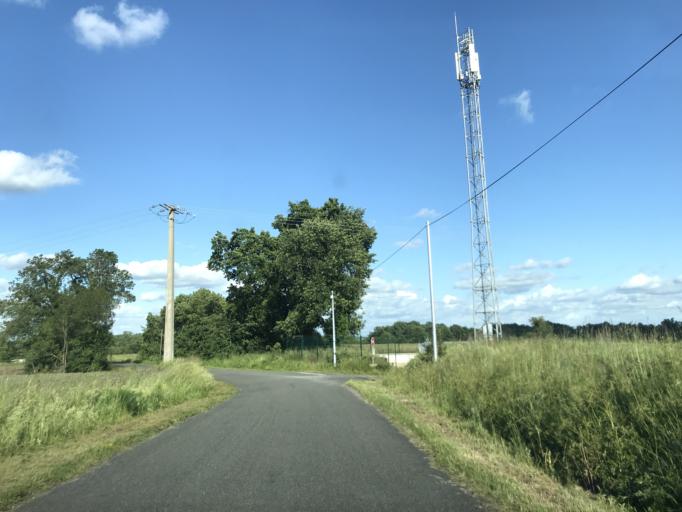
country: FR
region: Poitou-Charentes
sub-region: Departement de la Charente
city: Chalais
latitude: 45.2736
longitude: -0.0227
